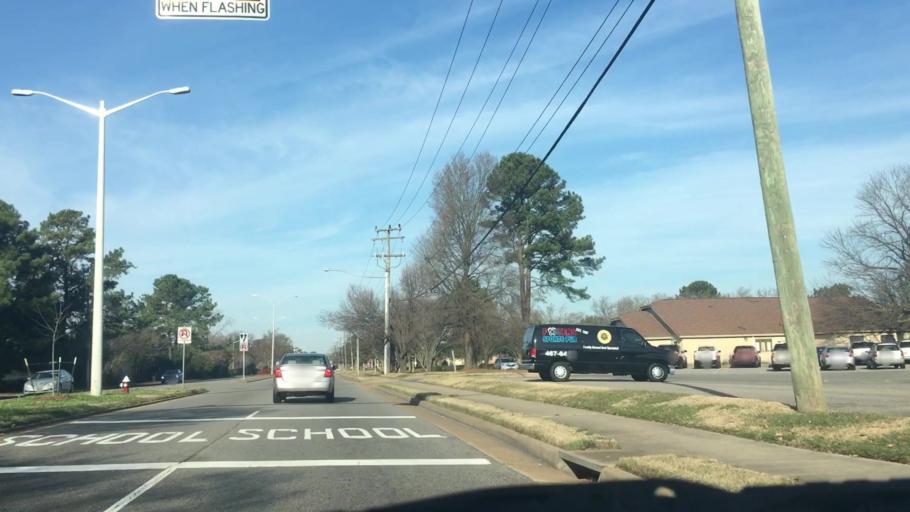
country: US
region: Virginia
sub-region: City of Chesapeake
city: Chesapeake
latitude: 36.8118
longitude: -76.1398
